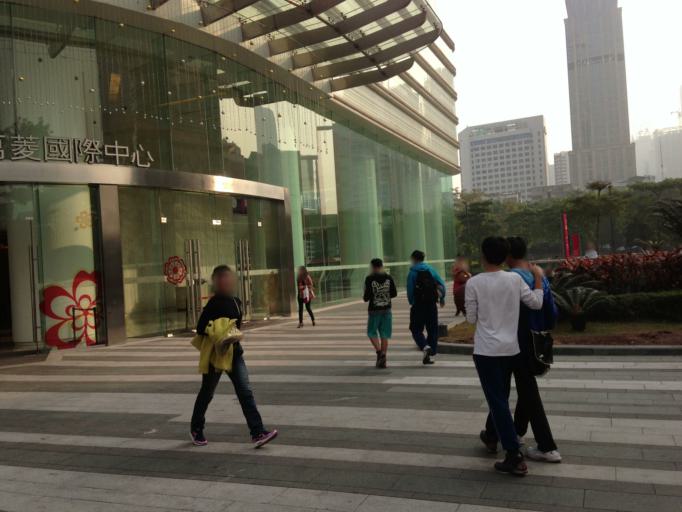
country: CN
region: Guangdong
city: Wushan
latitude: 23.1356
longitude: 113.3233
